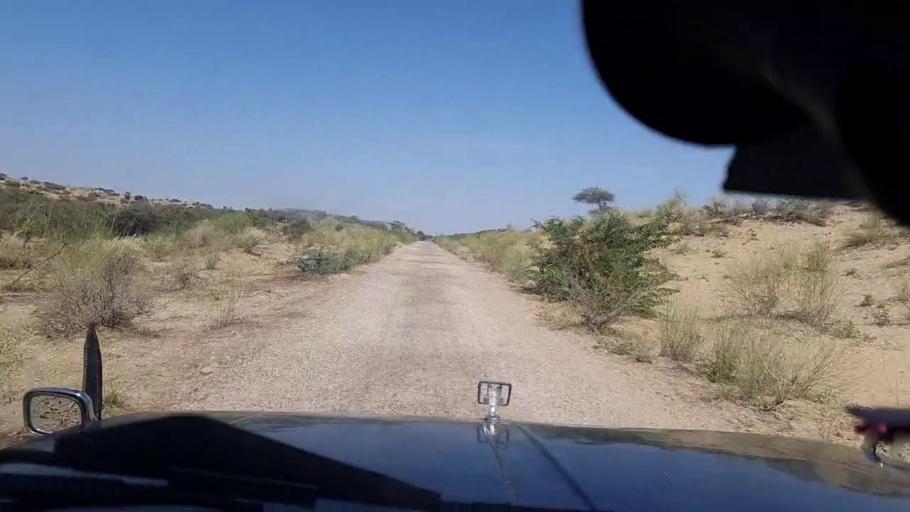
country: PK
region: Sindh
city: Diplo
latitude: 24.4096
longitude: 69.6437
